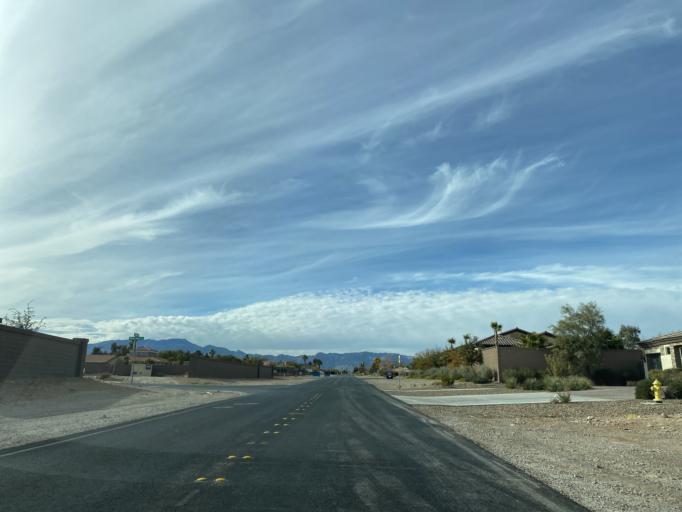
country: US
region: Nevada
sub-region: Clark County
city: Enterprise
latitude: 36.0338
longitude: -115.2572
